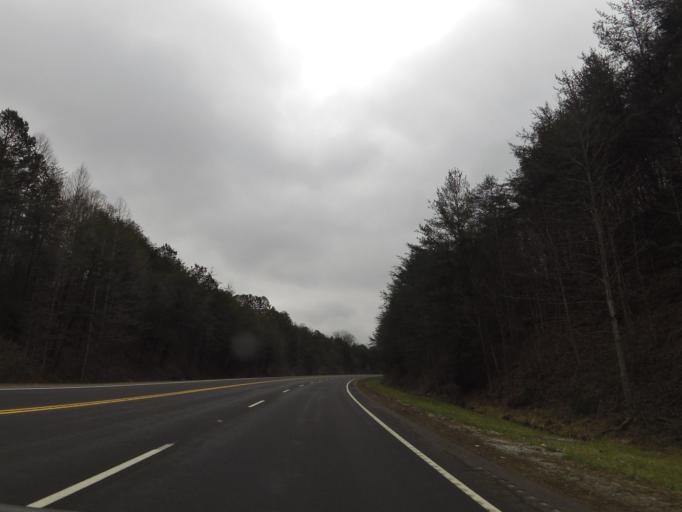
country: US
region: Tennessee
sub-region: Scott County
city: Huntsville
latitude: 36.4007
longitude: -84.4428
